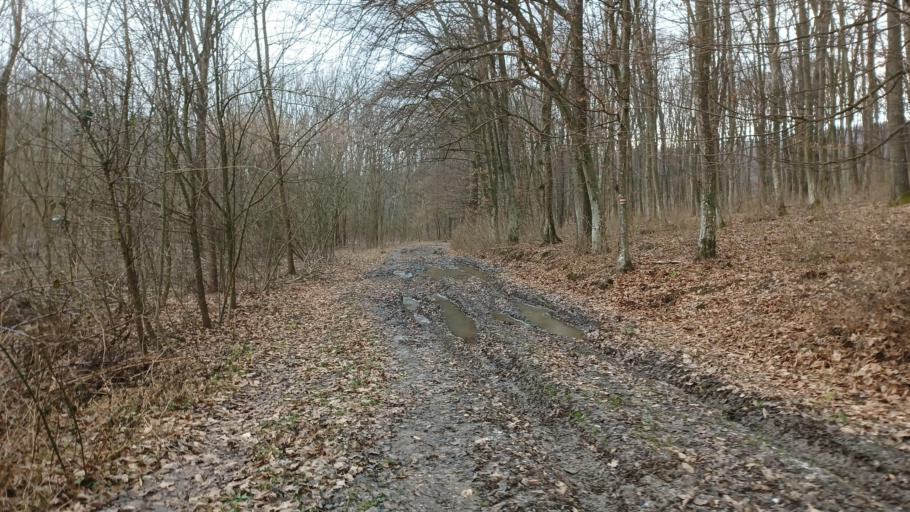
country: HU
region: Tolna
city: Szentgalpuszta
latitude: 46.3033
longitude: 18.6399
